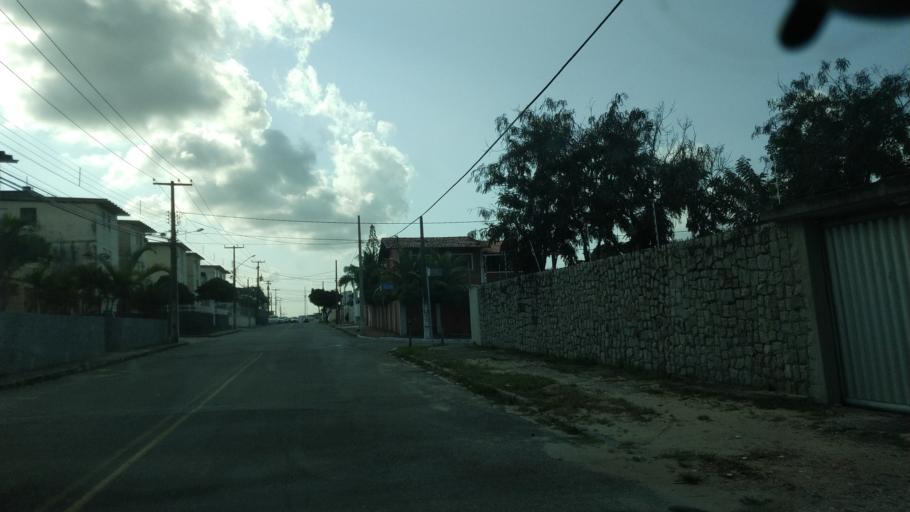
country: BR
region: Rio Grande do Norte
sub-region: Natal
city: Natal
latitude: -5.8625
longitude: -35.2028
